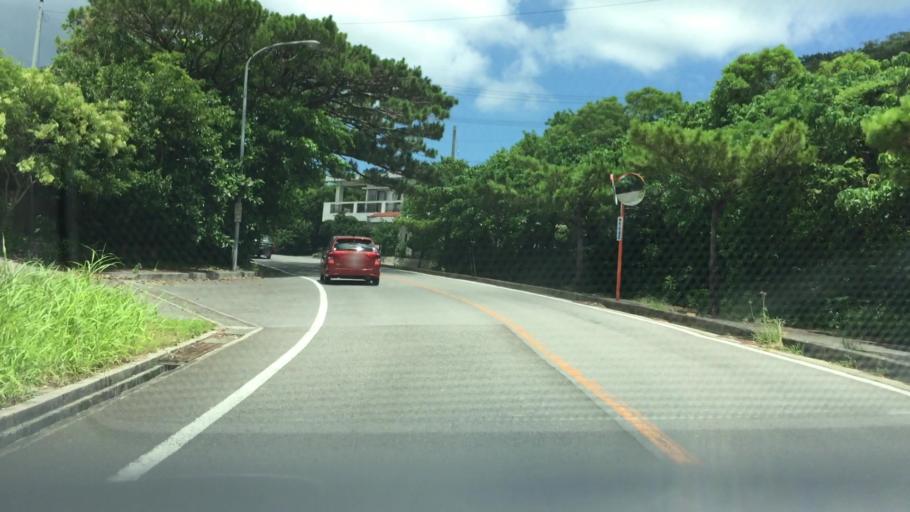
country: JP
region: Okinawa
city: Ishigaki
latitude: 24.4385
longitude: 124.1191
